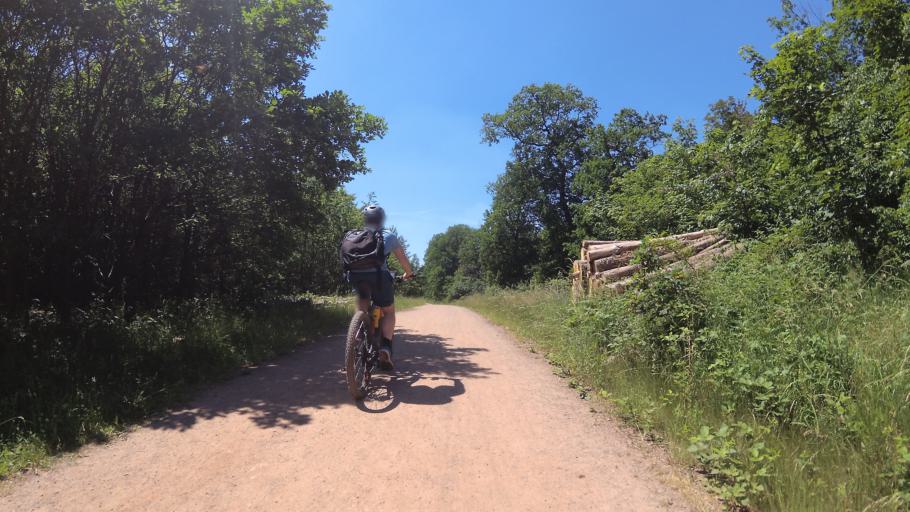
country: DE
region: Saarland
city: Saarwellingen
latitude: 49.3640
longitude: 6.8205
